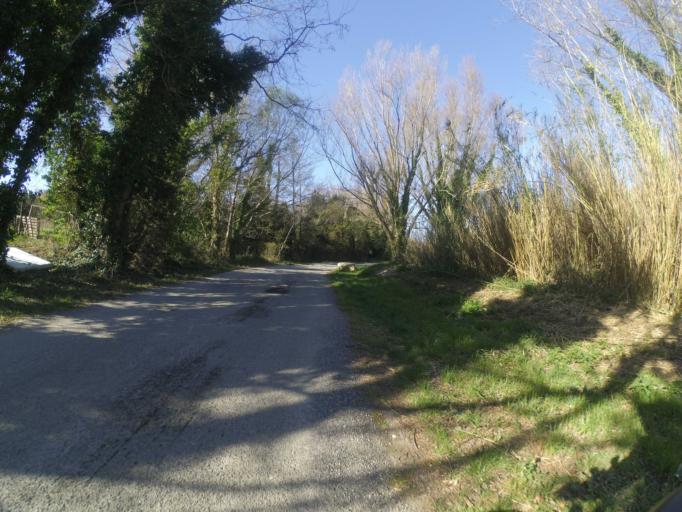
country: FR
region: Languedoc-Roussillon
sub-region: Departement des Pyrenees-Orientales
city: Millas
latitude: 42.6938
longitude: 2.6624
